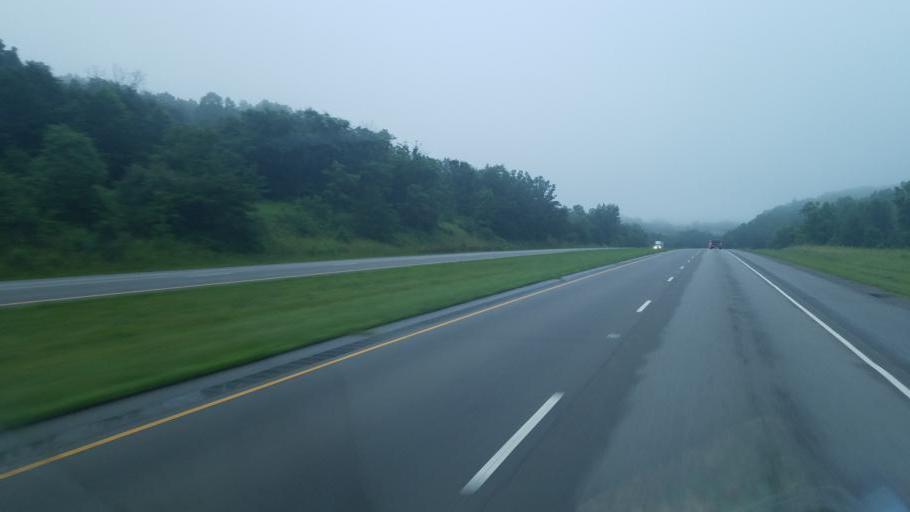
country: US
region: Ohio
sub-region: Jackson County
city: Oak Hill
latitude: 38.9416
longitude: -82.4735
